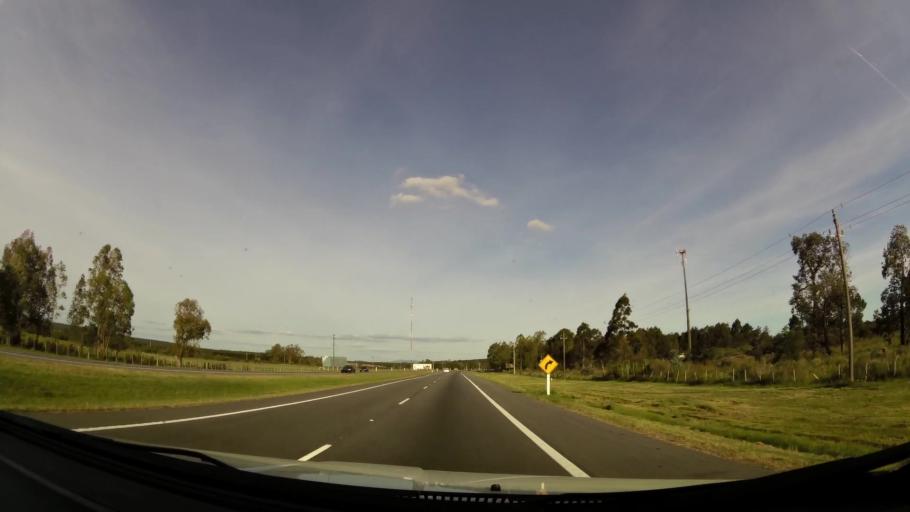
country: UY
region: Canelones
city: La Floresta
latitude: -34.7543
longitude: -55.6038
